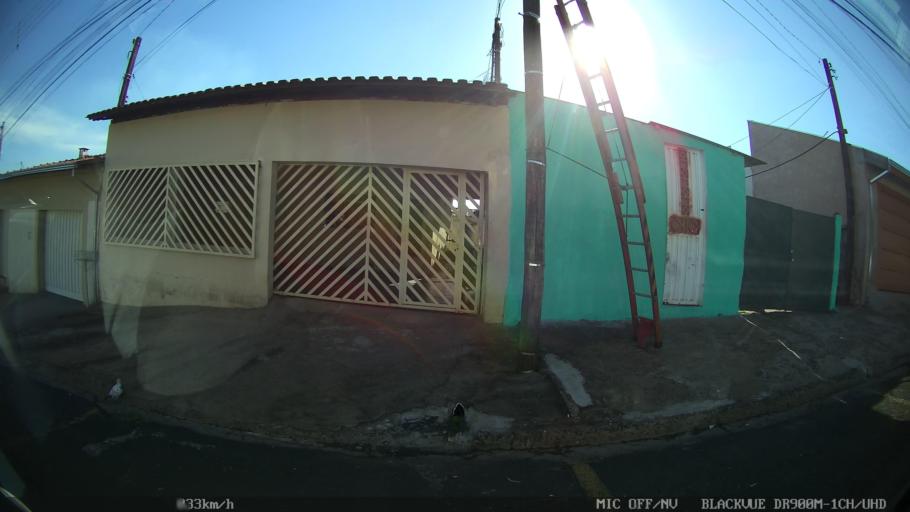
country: BR
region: Sao Paulo
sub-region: Franca
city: Franca
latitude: -20.5039
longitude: -47.4185
